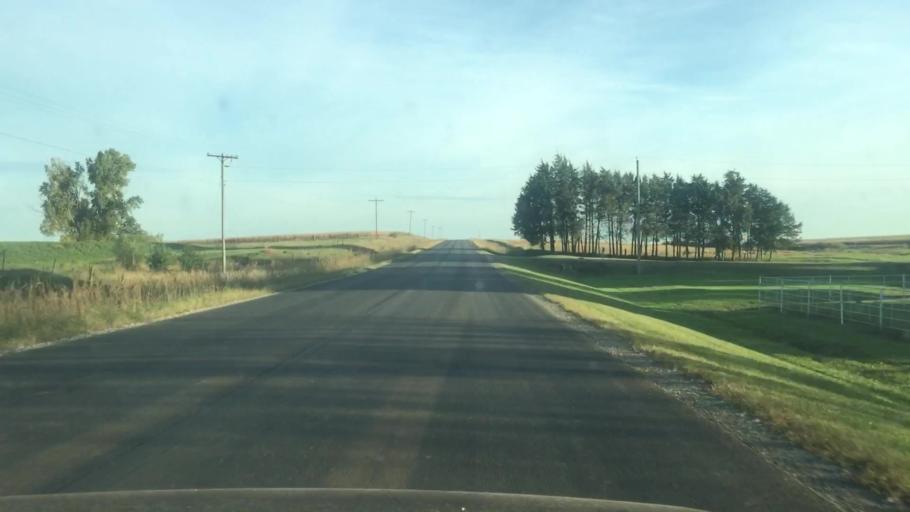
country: US
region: Kansas
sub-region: Marshall County
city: Marysville
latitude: 39.9007
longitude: -96.6010
